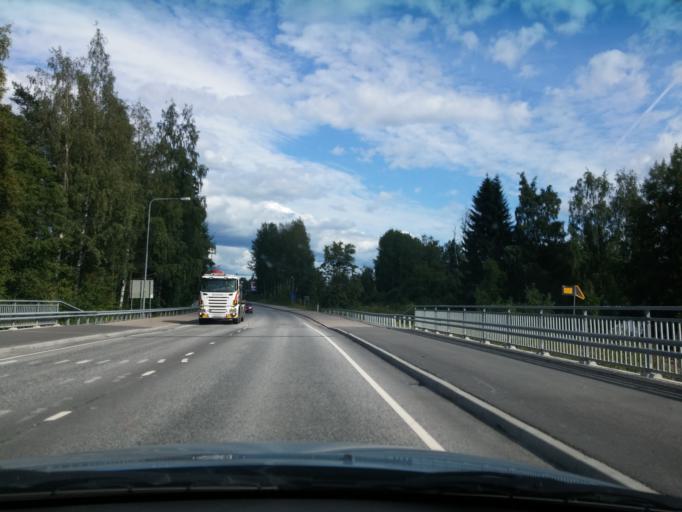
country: FI
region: Central Finland
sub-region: Keuruu
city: Keuruu
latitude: 62.2549
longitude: 24.7126
